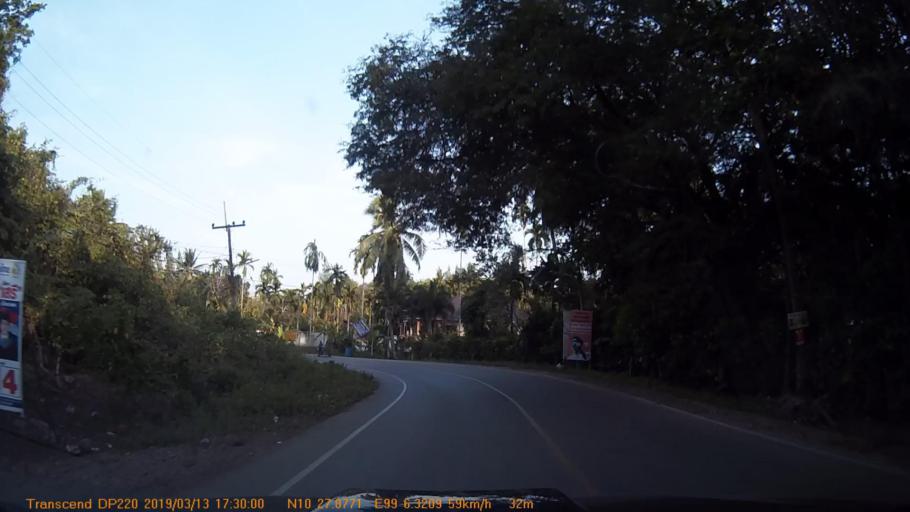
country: TH
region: Chumphon
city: Chumphon
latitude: 10.4645
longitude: 99.1056
